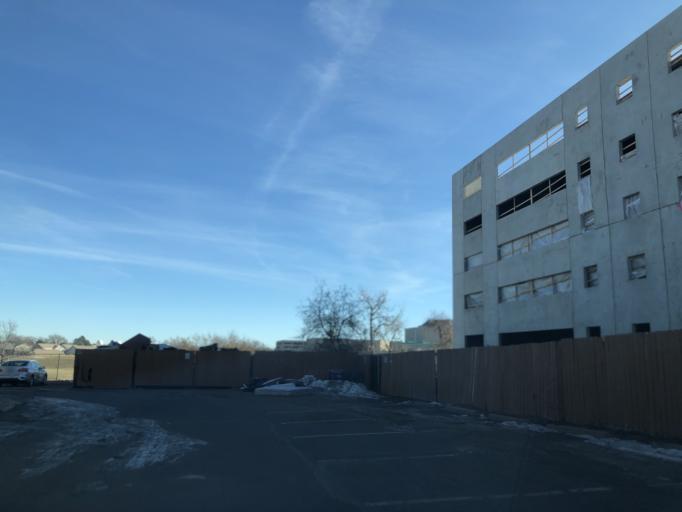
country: US
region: Colorado
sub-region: Adams County
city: Aurora
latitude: 39.7129
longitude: -104.8182
